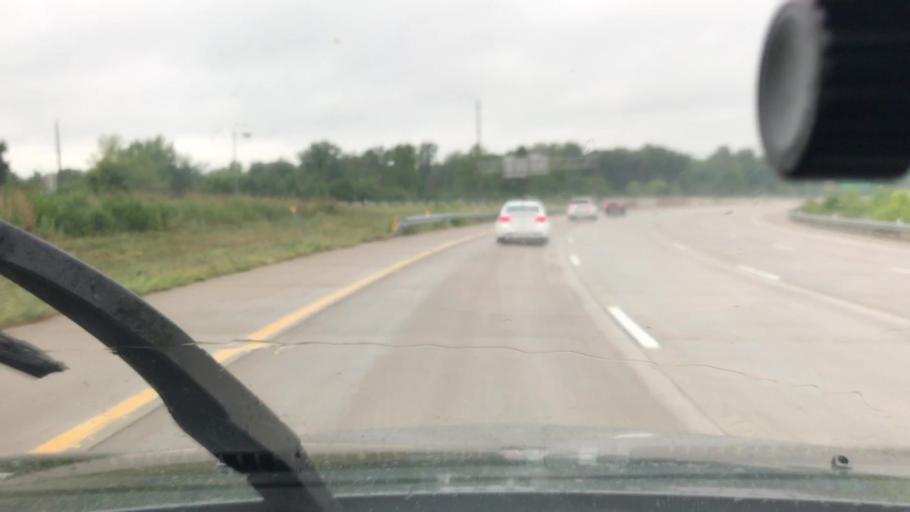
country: US
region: Missouri
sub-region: Saint Louis County
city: Maryland Heights
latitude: 38.6981
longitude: -90.4543
